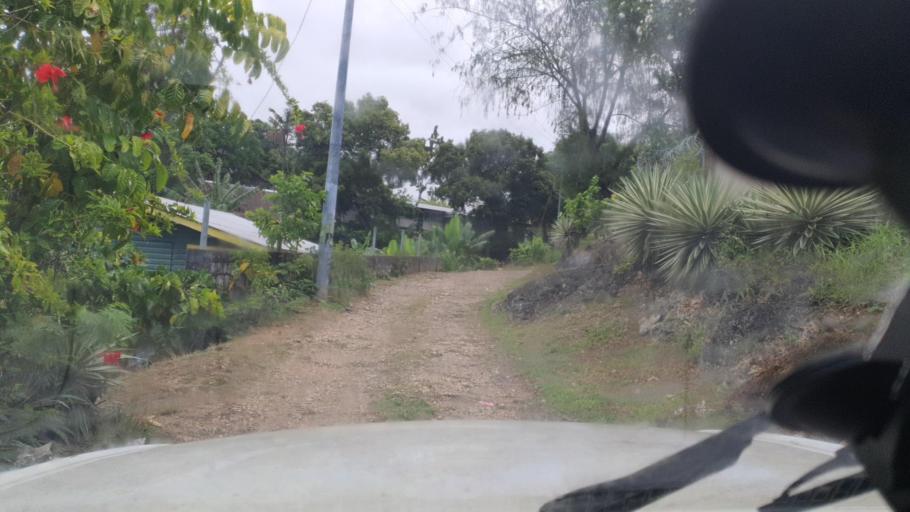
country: SB
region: Guadalcanal
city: Honiara
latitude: -9.4371
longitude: 159.9484
